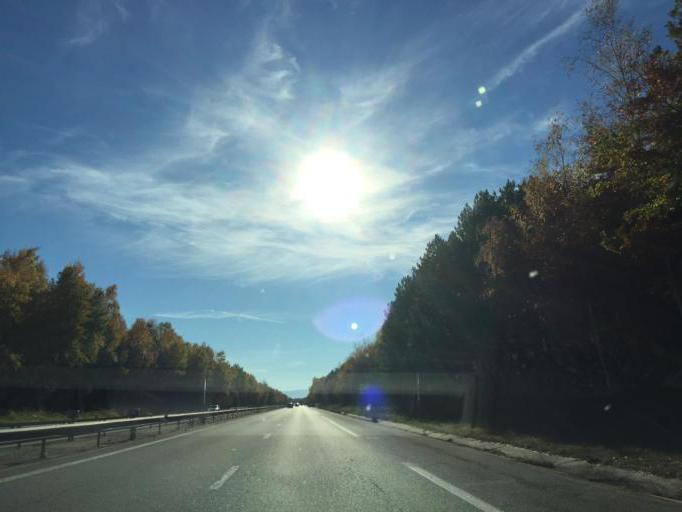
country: FR
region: Rhone-Alpes
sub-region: Departement de la Loire
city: Feurs
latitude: 45.7186
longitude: 4.1751
